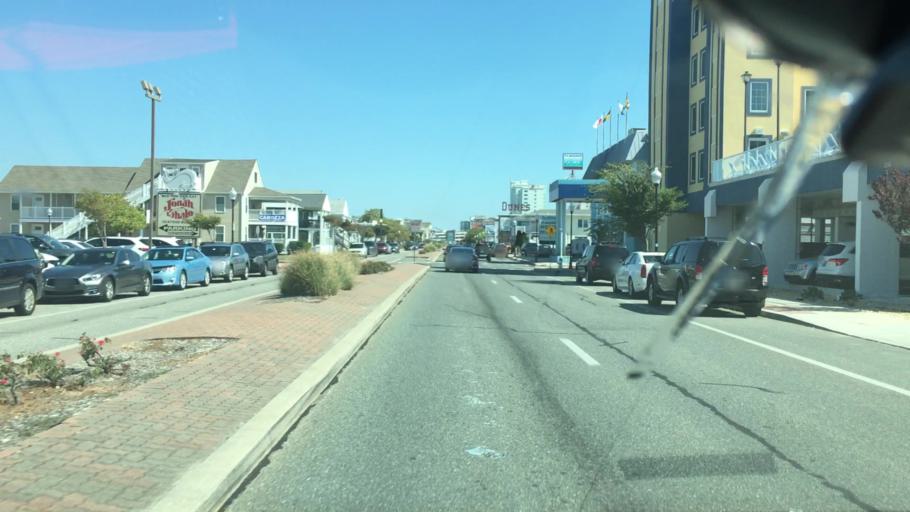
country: US
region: Maryland
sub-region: Worcester County
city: Ocean City
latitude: 38.3545
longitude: -75.0750
